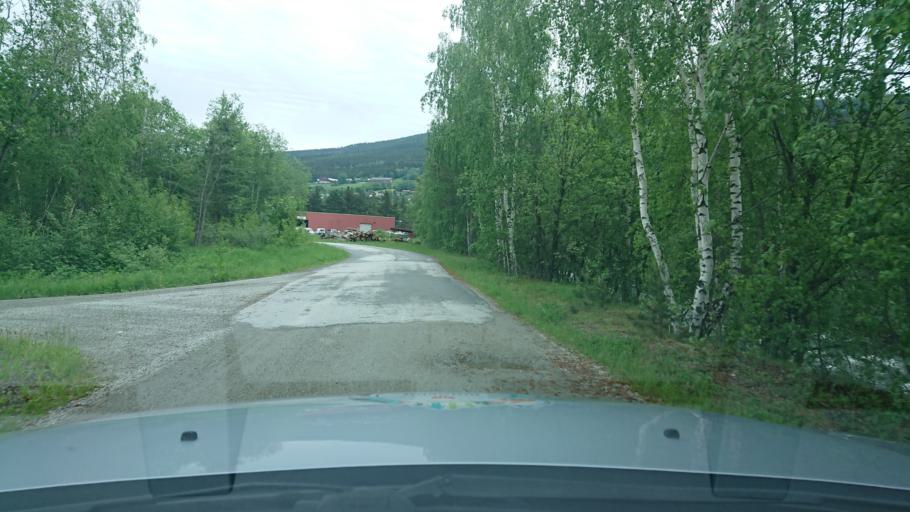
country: NO
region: Oppland
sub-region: Ringebu
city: Ringebu
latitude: 61.5247
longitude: 10.1386
